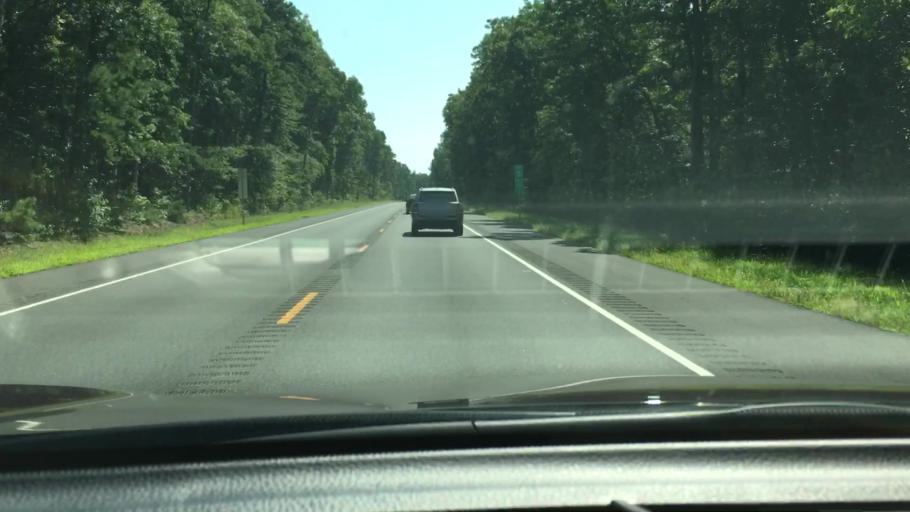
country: US
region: New Jersey
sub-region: Cape May County
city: Woodbine
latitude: 39.3170
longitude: -74.8401
